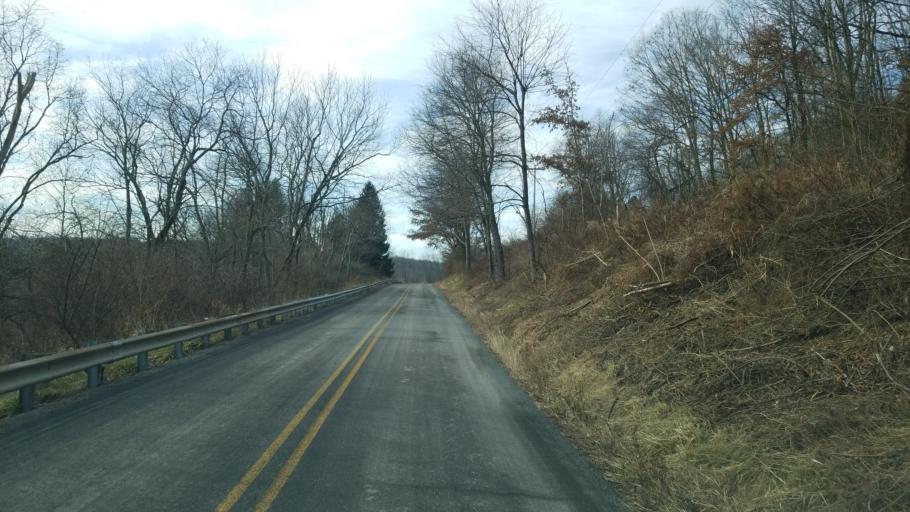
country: US
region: Pennsylvania
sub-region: Jefferson County
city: Punxsutawney
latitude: 40.8381
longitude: -79.1248
